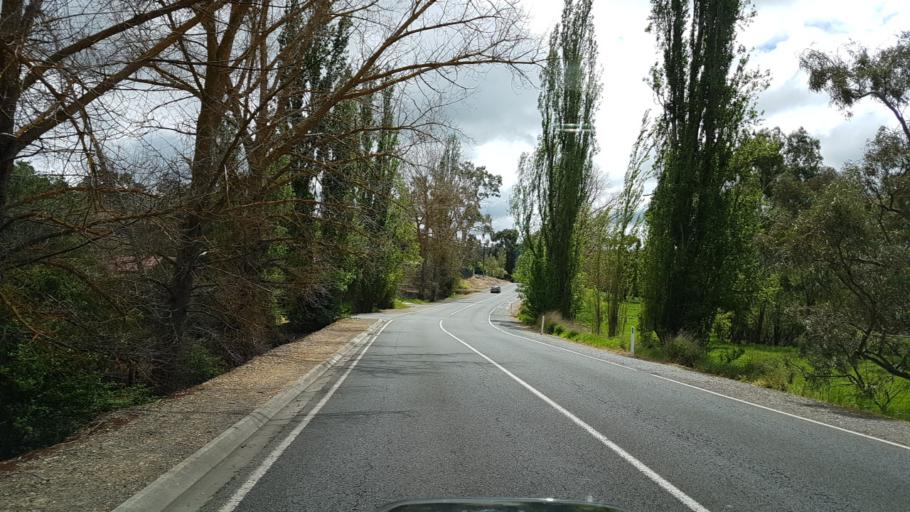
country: AU
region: South Australia
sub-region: Adelaide Hills
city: Gumeracha
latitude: -34.8282
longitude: 138.8878
